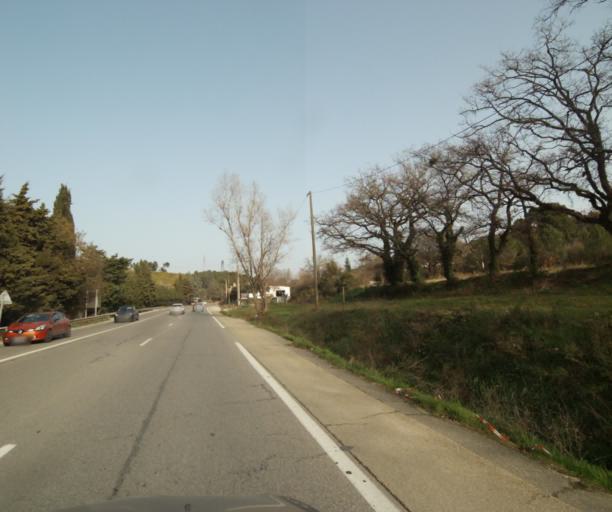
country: FR
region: Provence-Alpes-Cote d'Azur
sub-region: Departement des Bouches-du-Rhone
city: Les Pennes-Mirabeau
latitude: 43.4121
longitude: 5.3344
